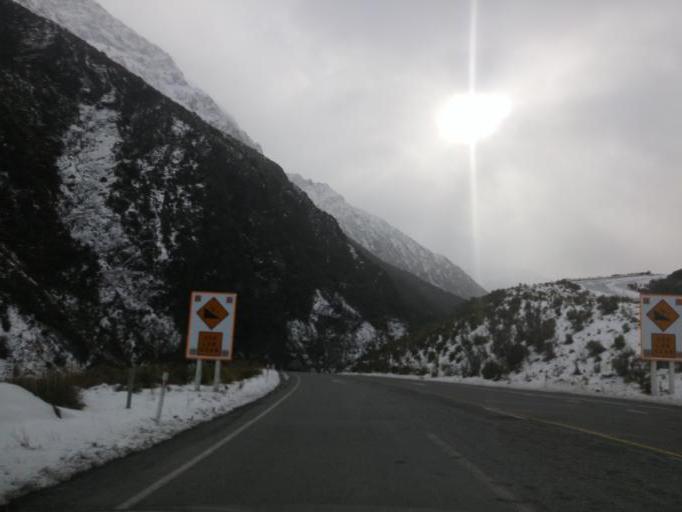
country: NZ
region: West Coast
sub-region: Grey District
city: Greymouth
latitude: -42.8899
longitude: 171.5565
